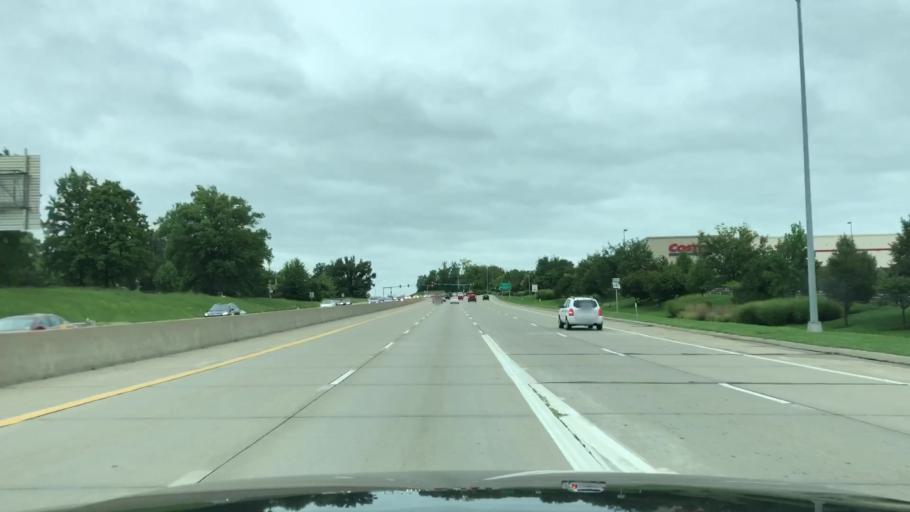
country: US
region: Missouri
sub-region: Saint Louis County
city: Manchester
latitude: 38.5955
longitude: -90.5086
